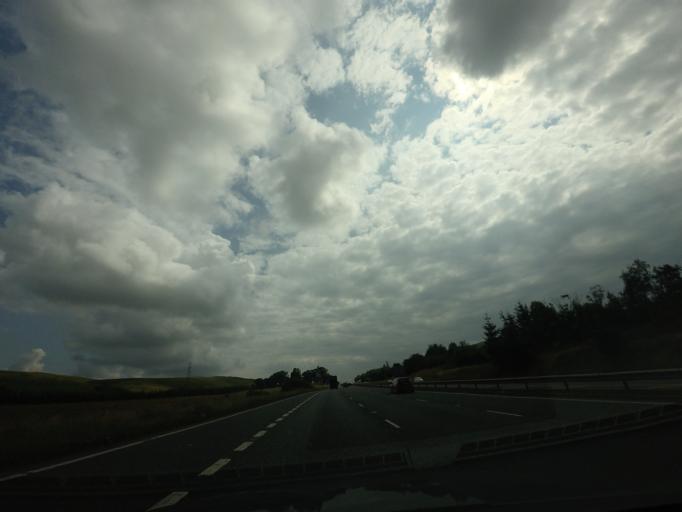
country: GB
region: Scotland
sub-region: South Lanarkshire
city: Douglas
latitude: 55.5705
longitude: -3.8091
